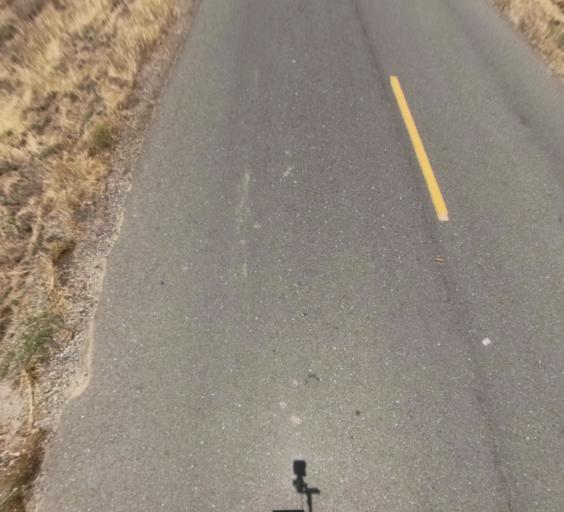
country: US
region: California
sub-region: Madera County
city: Madera Acres
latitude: 37.0499
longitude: -119.9958
